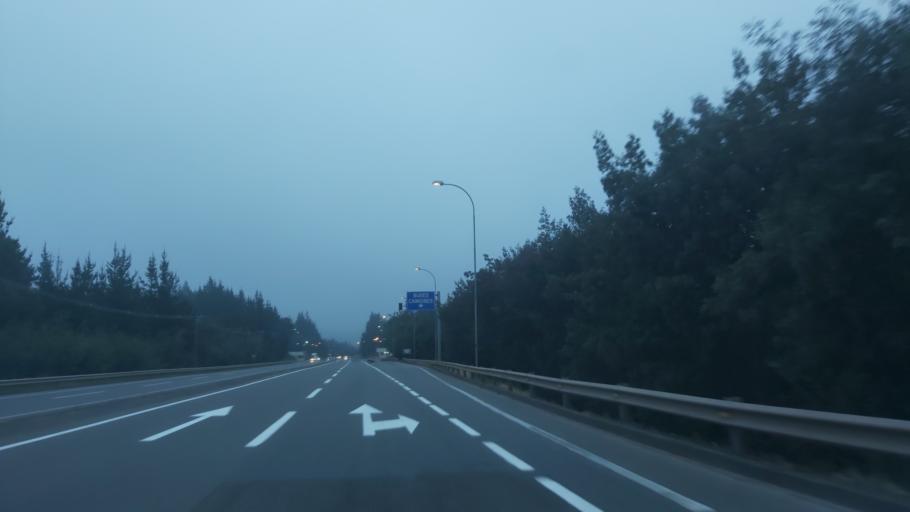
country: CL
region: Biobio
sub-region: Provincia de Concepcion
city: Penco
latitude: -36.7339
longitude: -72.8850
